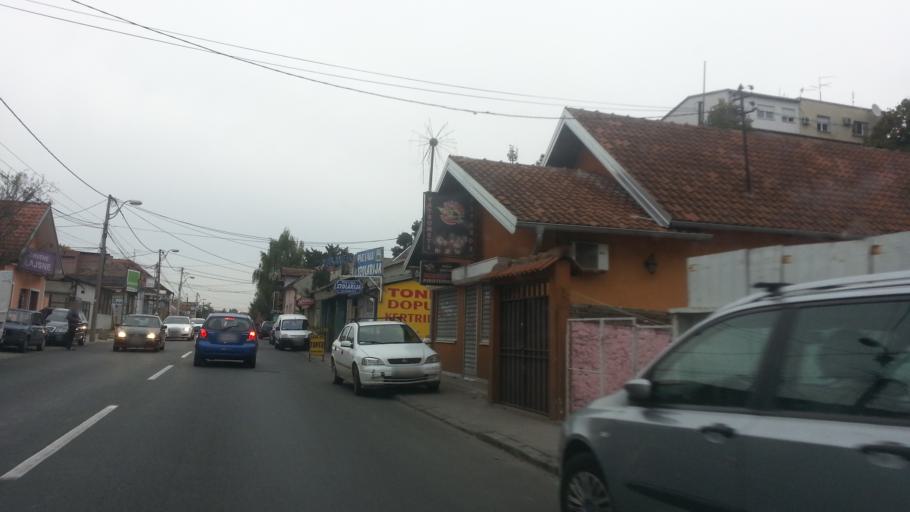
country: RS
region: Central Serbia
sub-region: Belgrade
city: Zemun
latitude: 44.8326
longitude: 20.4004
